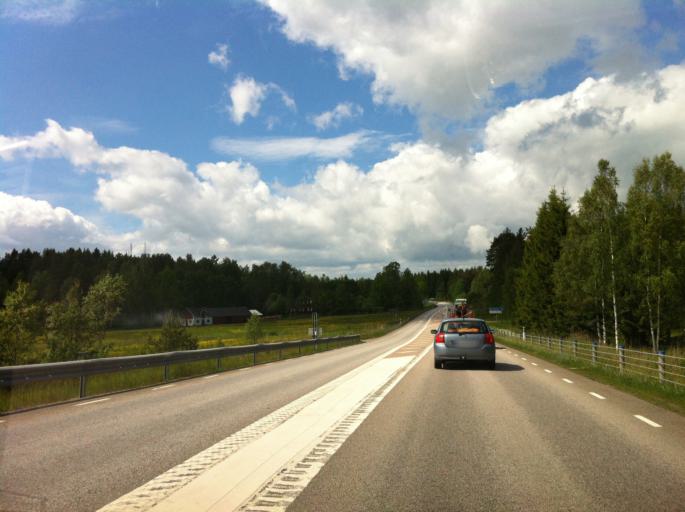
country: SE
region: Vaermland
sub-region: Saffle Kommun
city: Saeffle
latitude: 59.1521
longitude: 12.9683
